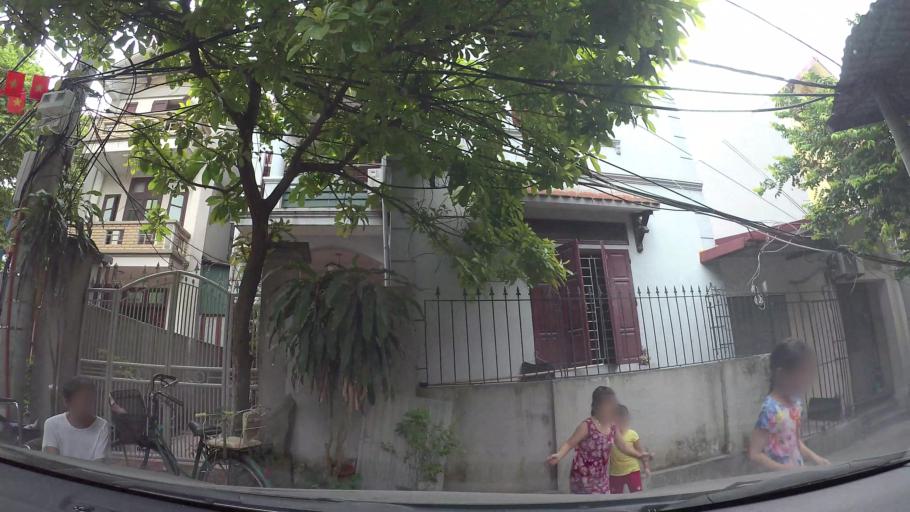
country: VN
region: Ha Noi
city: Trau Quy
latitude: 21.0747
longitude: 105.9169
